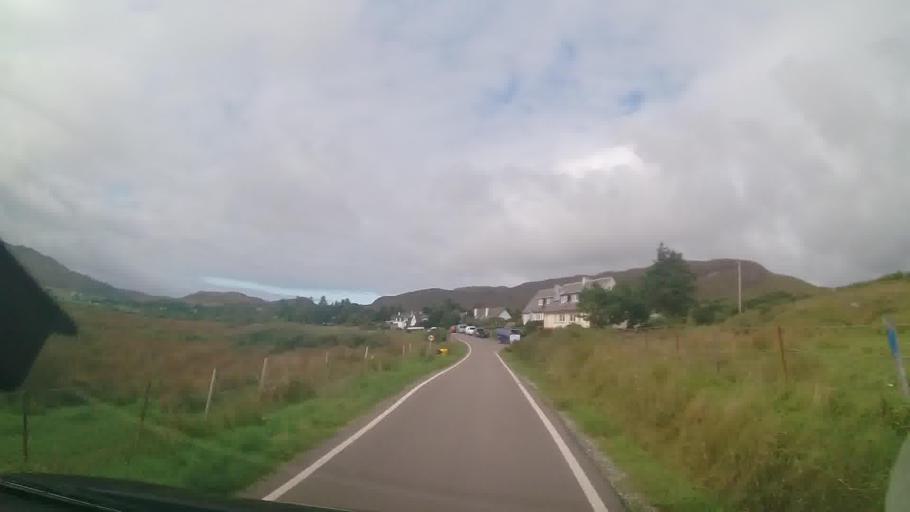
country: GB
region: Scotland
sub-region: Argyll and Bute
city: Isle Of Mull
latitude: 56.6925
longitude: -6.0947
